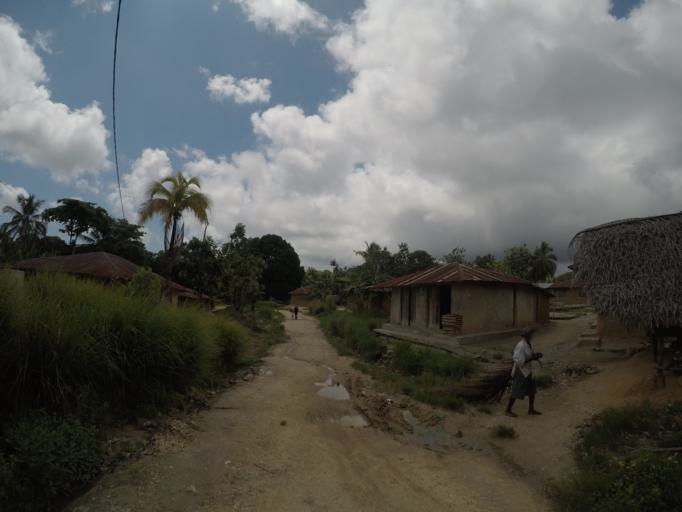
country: TZ
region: Pemba South
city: Mtambile
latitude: -5.3938
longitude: 39.7398
